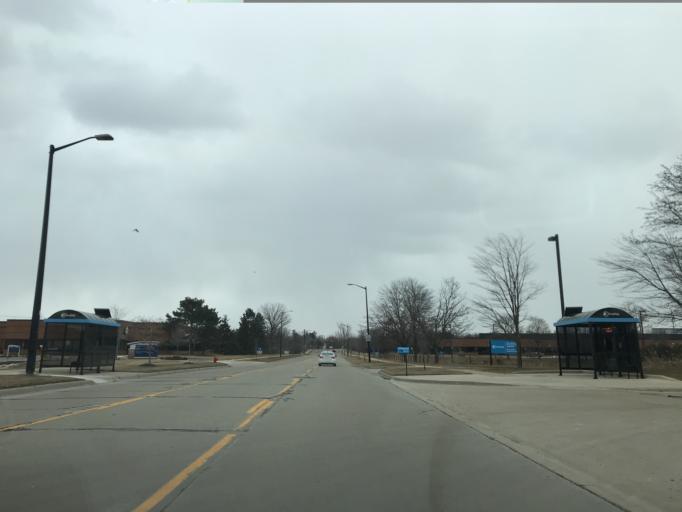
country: US
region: Michigan
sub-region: Washtenaw County
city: Ann Arbor
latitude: 42.2476
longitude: -83.7312
